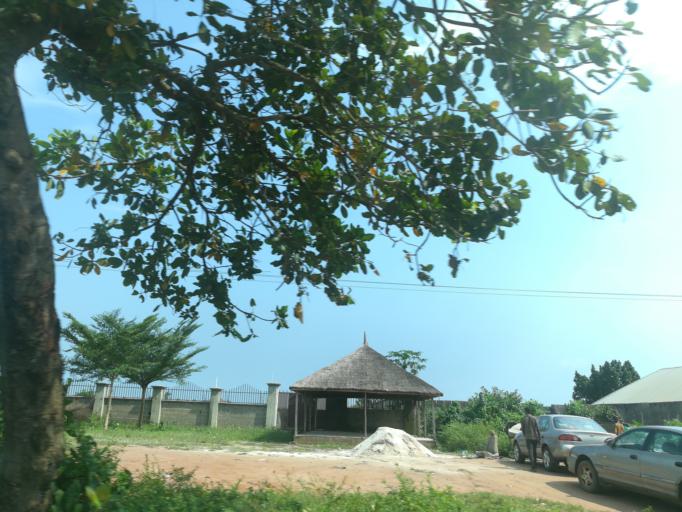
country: NG
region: Lagos
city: Ikorodu
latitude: 6.6069
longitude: 3.6288
